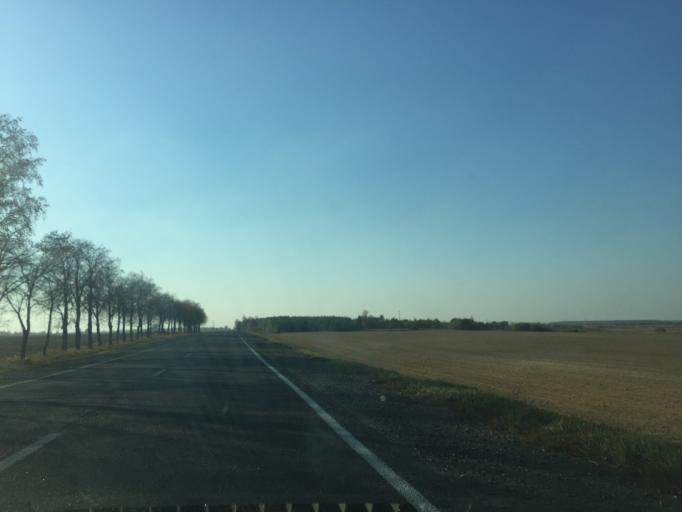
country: BY
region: Gomel
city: Dobrush
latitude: 52.3852
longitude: 31.3985
